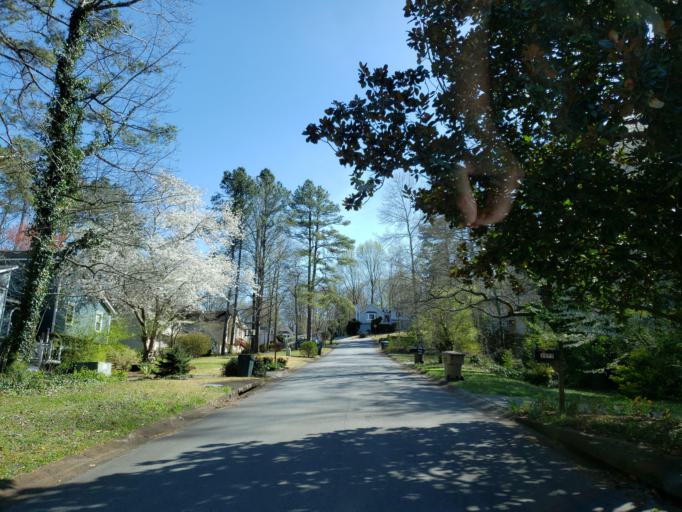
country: US
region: Georgia
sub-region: Cherokee County
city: Woodstock
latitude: 34.0375
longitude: -84.4914
